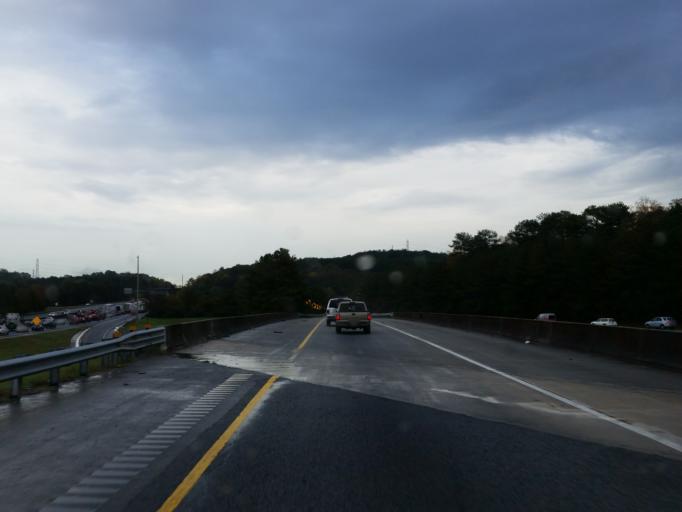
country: US
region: Georgia
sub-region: Clayton County
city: Conley
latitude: 33.6694
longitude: -84.3353
